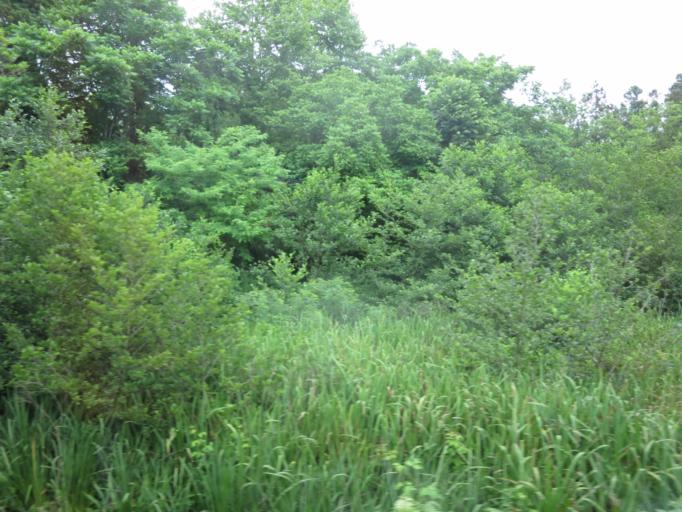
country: GE
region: Guria
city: Urek'i
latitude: 42.0114
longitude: 41.7782
